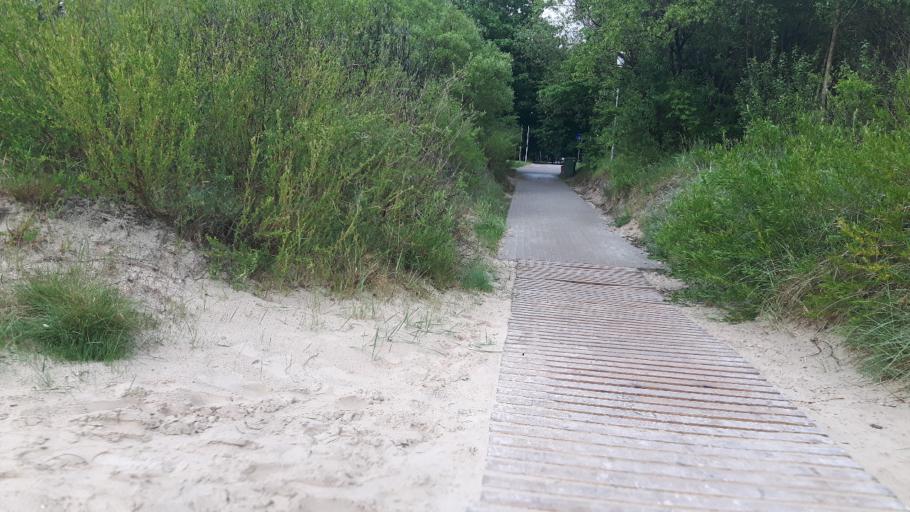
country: LV
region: Liepaja
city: Liepaja
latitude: 56.5075
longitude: 20.9919
